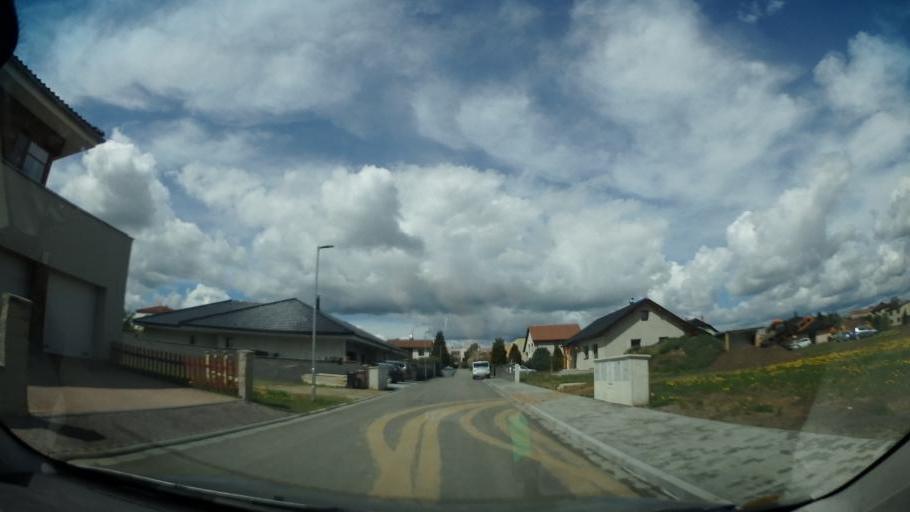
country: CZ
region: Vysocina
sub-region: Okres Zd'ar nad Sazavou
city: Velka Bites
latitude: 49.2919
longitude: 16.2322
